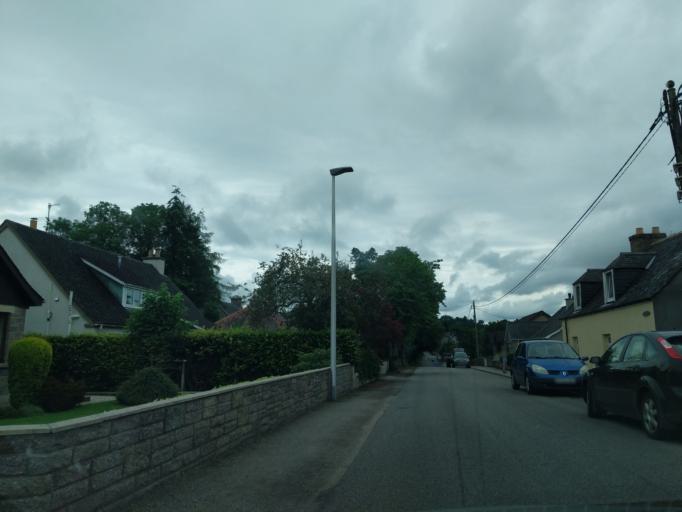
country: GB
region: Scotland
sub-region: Moray
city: Rothes
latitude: 57.4708
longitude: -3.2228
